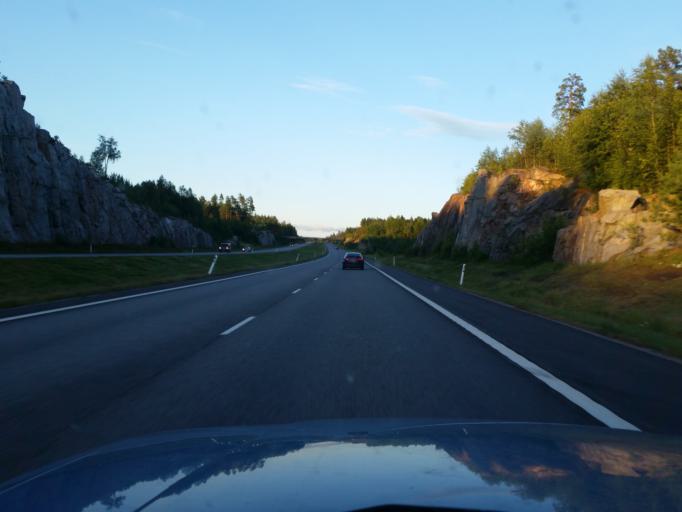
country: FI
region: Varsinais-Suomi
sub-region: Loimaa
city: Marttila
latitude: 60.4281
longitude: 22.8576
